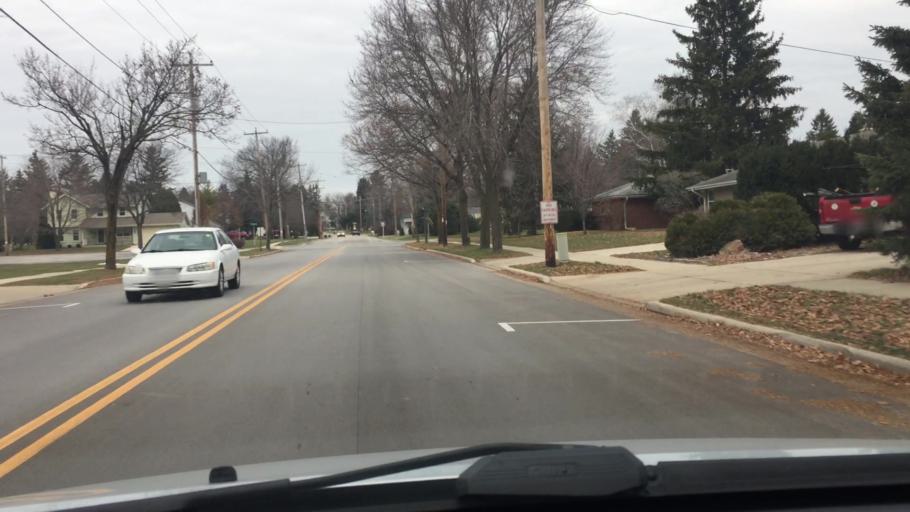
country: US
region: Wisconsin
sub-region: Ozaukee County
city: Thiensville
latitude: 43.2366
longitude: -87.9808
